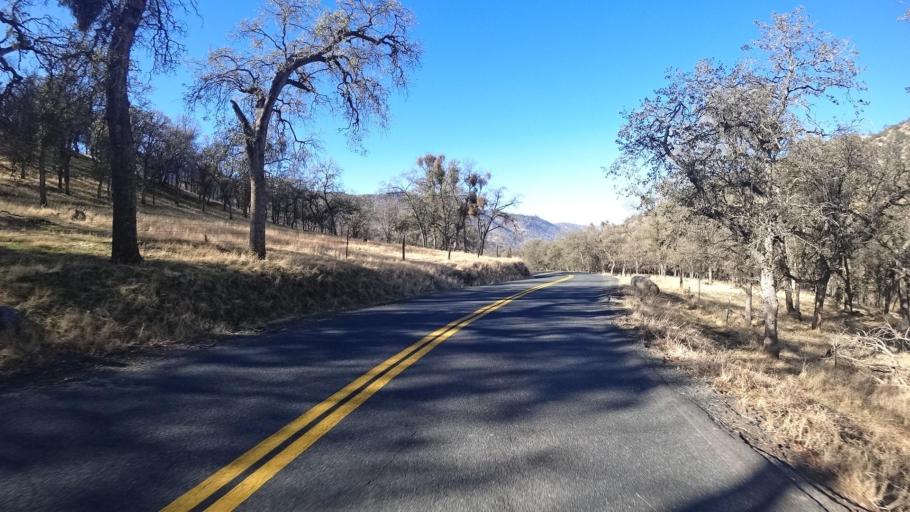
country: US
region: California
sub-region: Kern County
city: Alta Sierra
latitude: 35.7861
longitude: -118.7713
